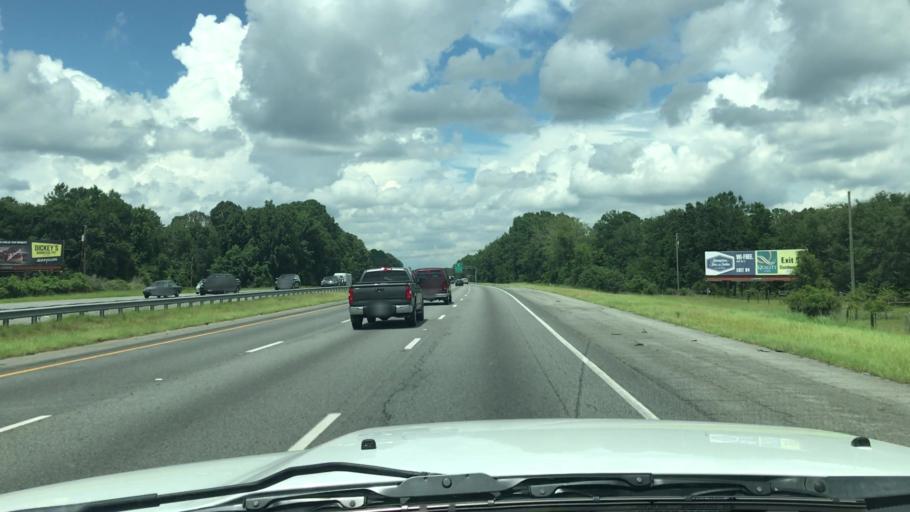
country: US
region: Georgia
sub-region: Bryan County
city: Richmond Hill
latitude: 31.9929
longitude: -81.2945
